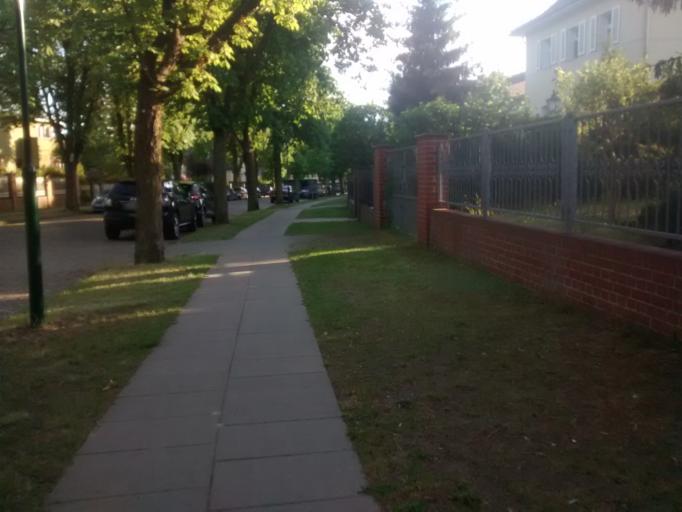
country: DE
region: Brandenburg
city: Hohen Neuendorf
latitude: 52.6705
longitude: 13.2899
